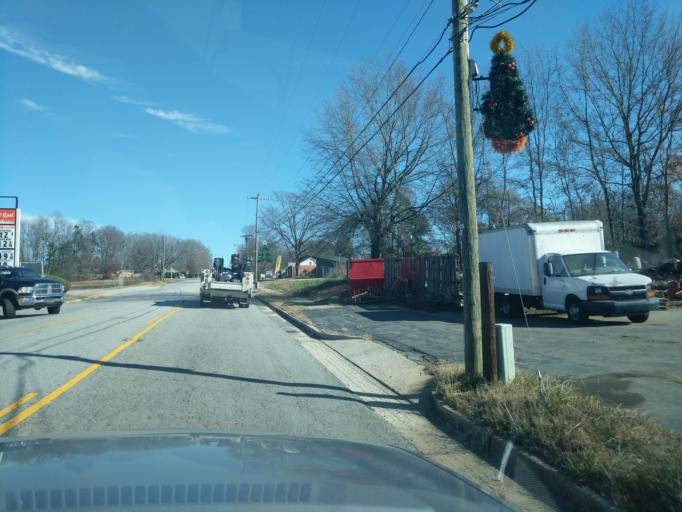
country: US
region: South Carolina
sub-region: Spartanburg County
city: Mayo
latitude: 35.1509
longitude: -81.8596
